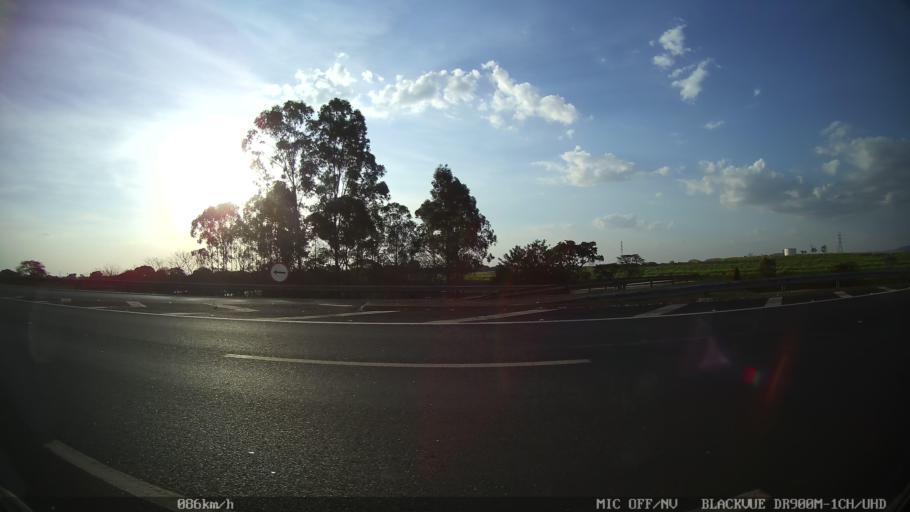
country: BR
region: Sao Paulo
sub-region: Ribeirao Preto
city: Ribeirao Preto
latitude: -21.1122
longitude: -47.7794
